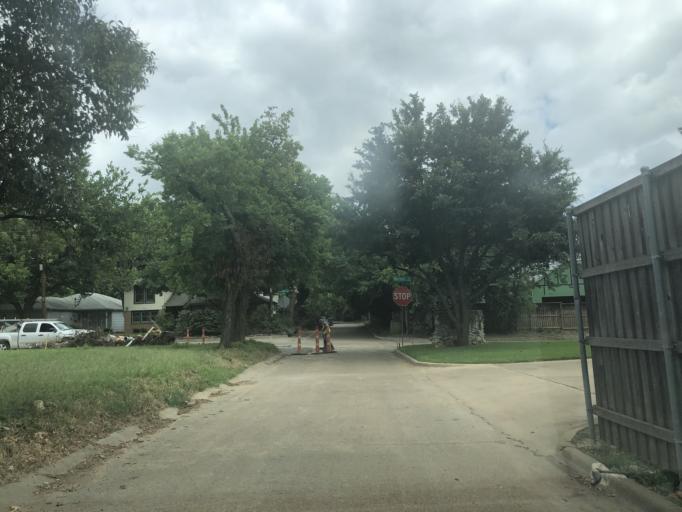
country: US
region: Texas
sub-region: Dallas County
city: University Park
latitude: 32.8873
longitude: -96.8327
